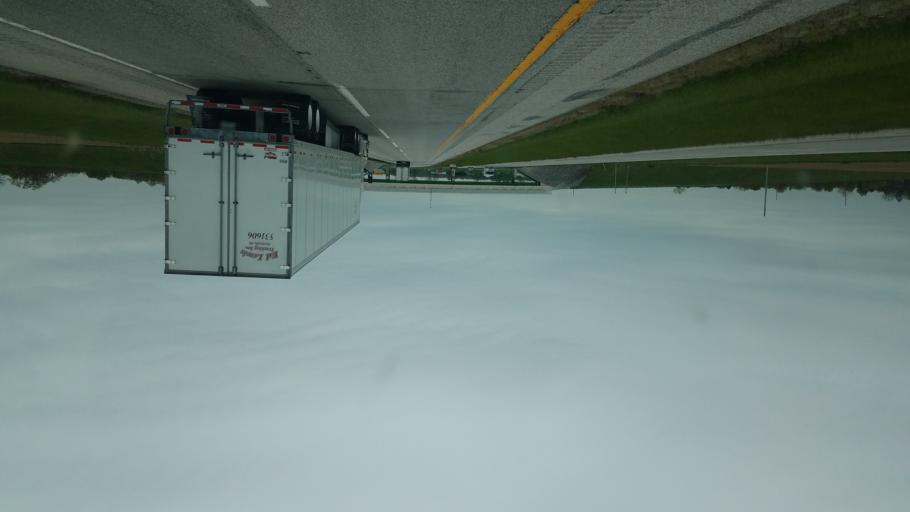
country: US
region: Michigan
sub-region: Saint Joseph County
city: Sturgis
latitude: 41.7483
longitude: -85.4981
